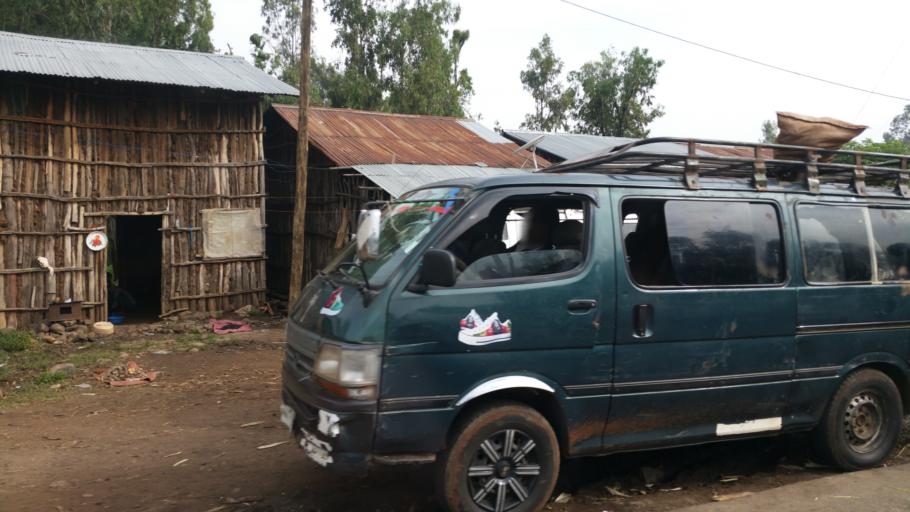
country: ET
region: Amhara
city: Werota
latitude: 11.8371
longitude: 37.6336
